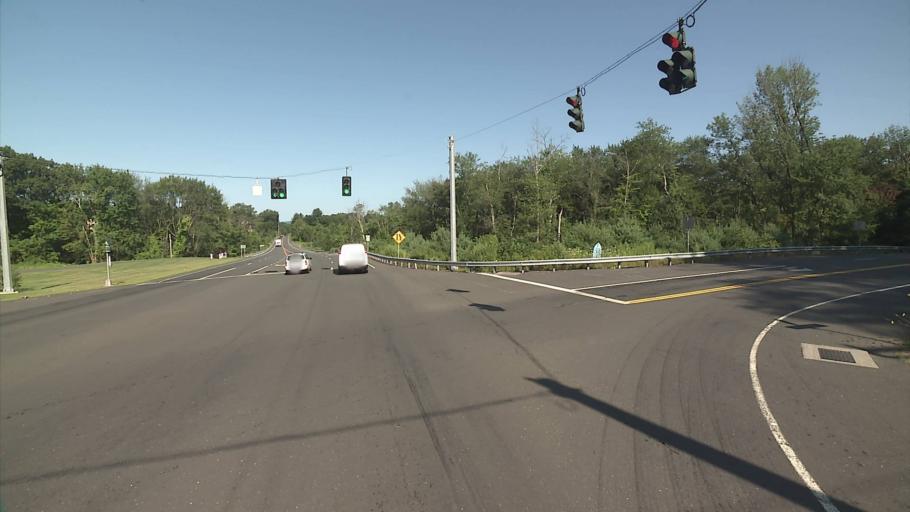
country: US
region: Connecticut
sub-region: Hartford County
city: Tariffville
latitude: 41.9469
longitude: -72.7400
